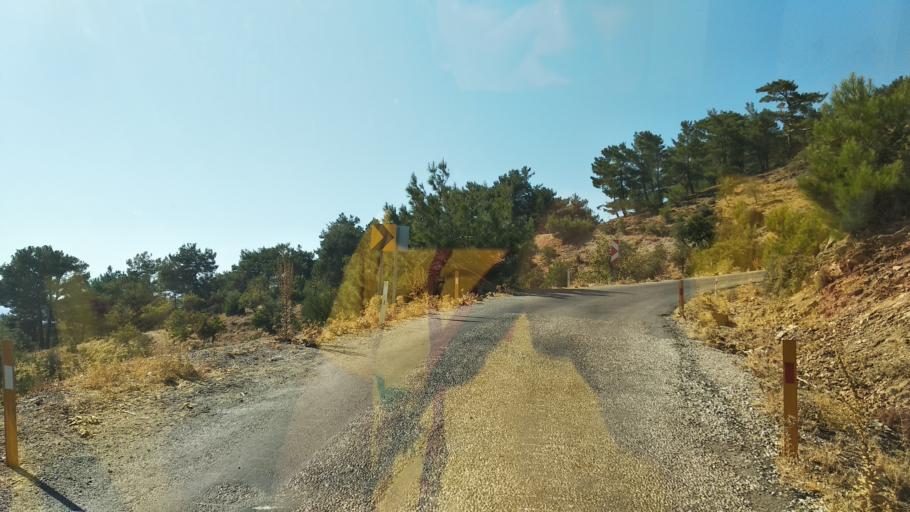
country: TR
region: Izmir
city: Gaziemir
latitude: 38.2952
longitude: 27.0009
